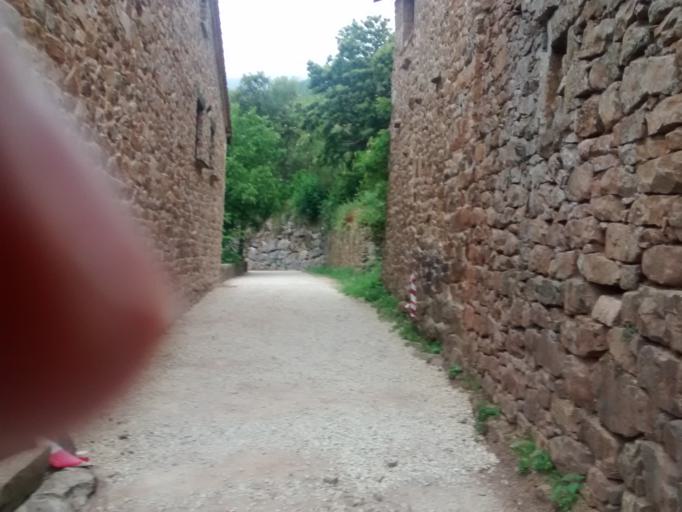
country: ES
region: Cantabria
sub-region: Provincia de Cantabria
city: Pesquera
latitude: 43.1448
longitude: -4.1938
